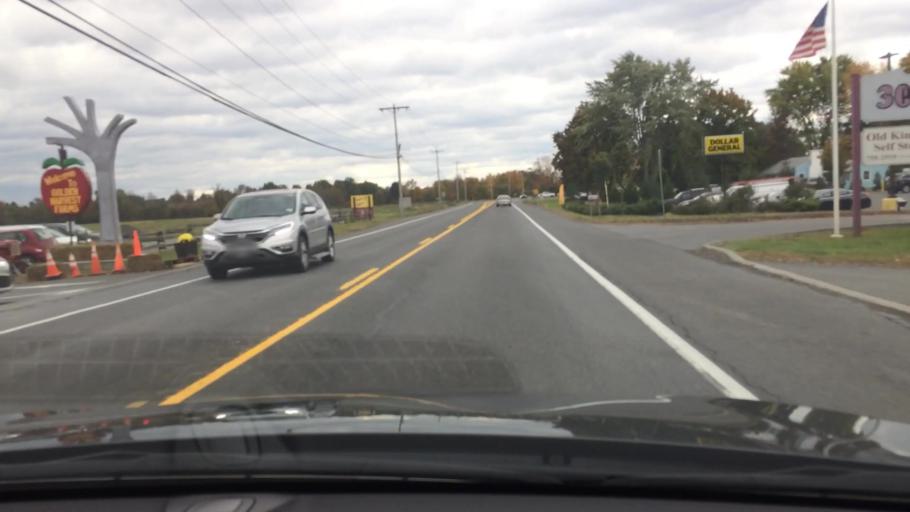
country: US
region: New York
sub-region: Columbia County
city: Valatie
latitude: 42.4352
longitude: -73.6871
